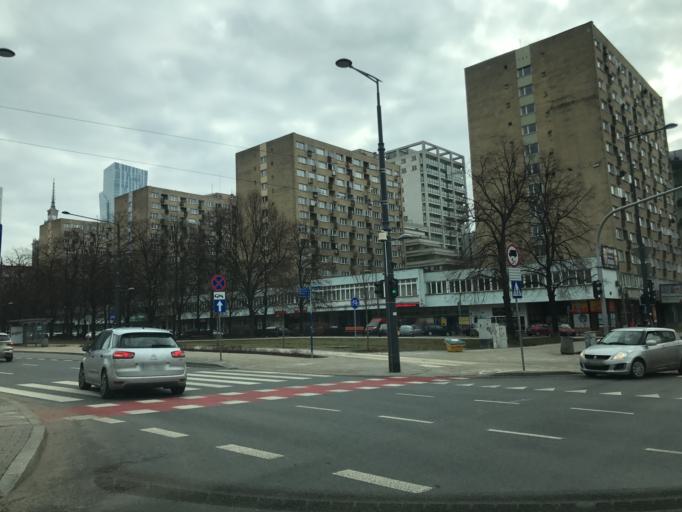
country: PL
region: Masovian Voivodeship
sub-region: Warszawa
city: Wola
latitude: 52.2319
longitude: 20.9925
